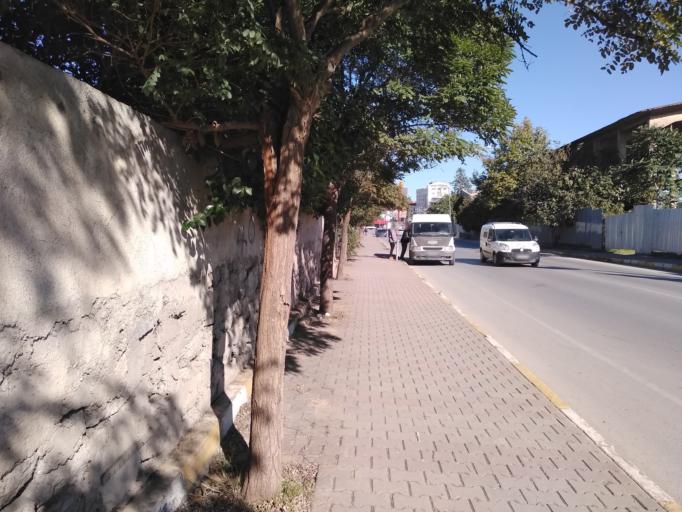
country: TR
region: Istanbul
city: Maltepe
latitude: 40.9141
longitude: 29.1386
